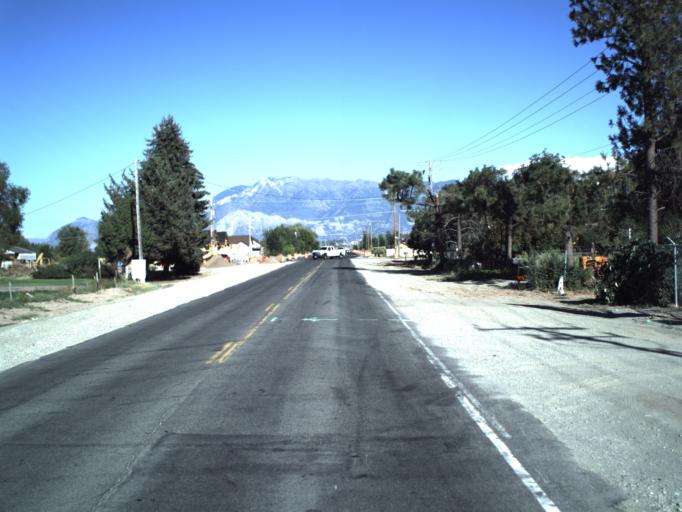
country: US
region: Utah
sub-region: Weber County
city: Hooper
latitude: 41.1907
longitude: -112.1045
